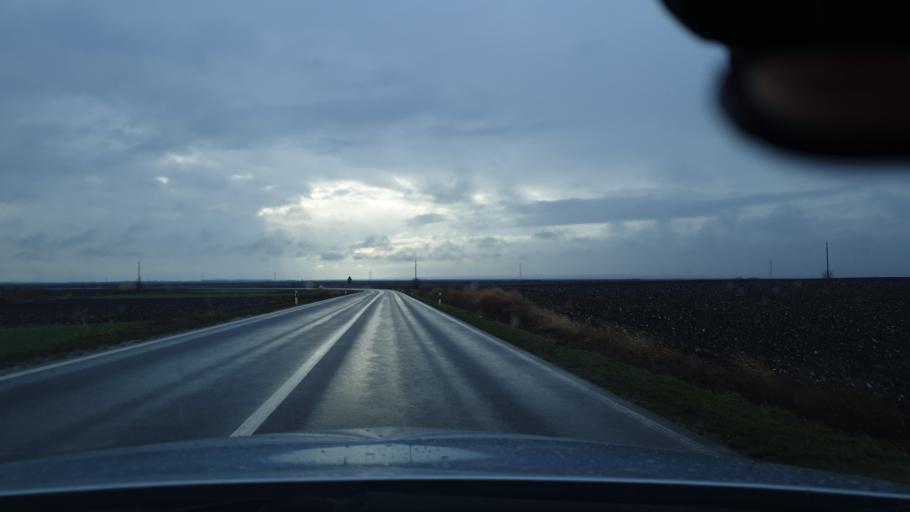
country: RS
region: Autonomna Pokrajina Vojvodina
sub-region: Juznobanatski Okrug
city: Kovin
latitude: 44.8141
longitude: 20.8563
